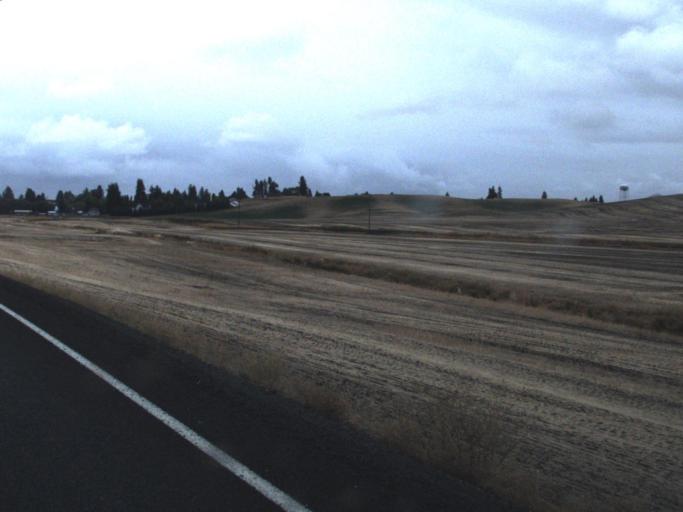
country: US
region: Washington
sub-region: Whitman County
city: Colfax
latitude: 47.1409
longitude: -117.2484
